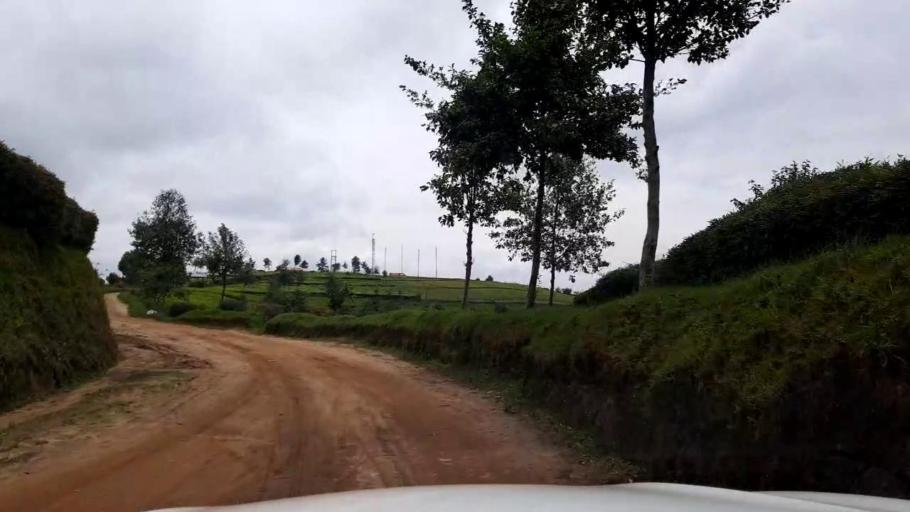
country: RW
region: Western Province
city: Kibuye
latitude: -1.9526
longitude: 29.4122
